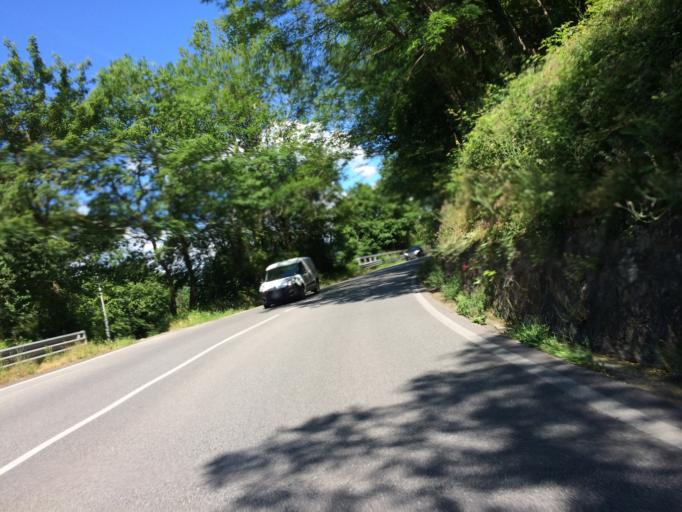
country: IT
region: Tuscany
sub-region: Provincia di Massa-Carrara
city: Terrarossa
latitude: 44.2467
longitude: 9.9592
